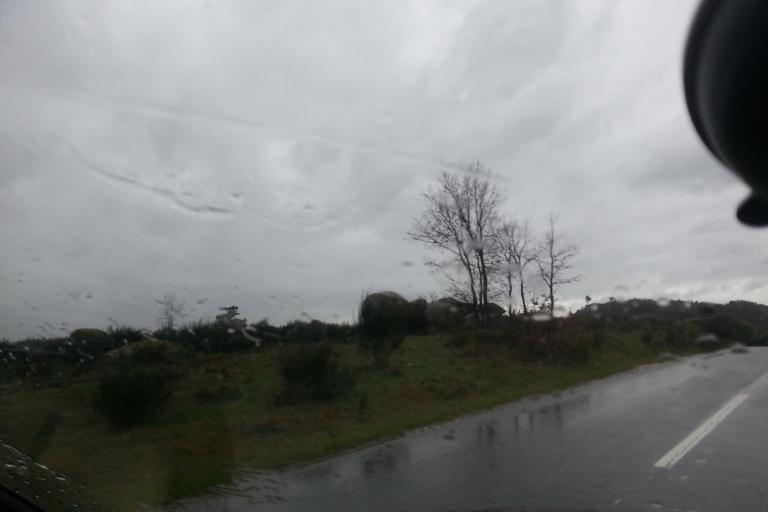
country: PT
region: Guarda
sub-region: Fornos de Algodres
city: Fornos de Algodres
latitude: 40.5769
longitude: -7.5103
